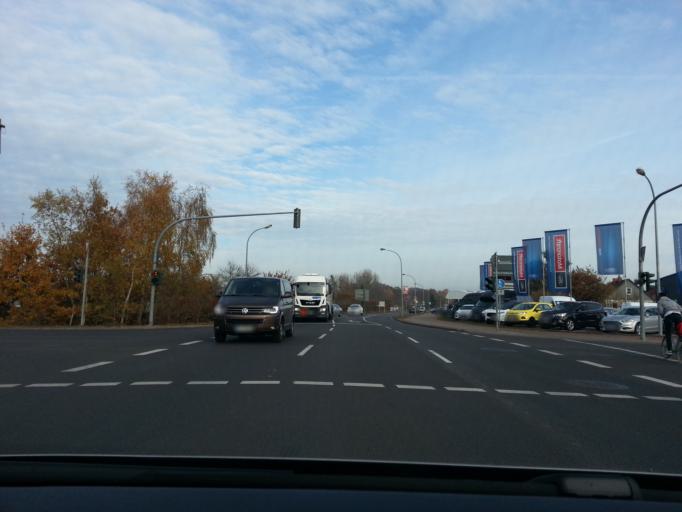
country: DE
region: Mecklenburg-Vorpommern
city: Torgelow
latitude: 53.6356
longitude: 14.0274
